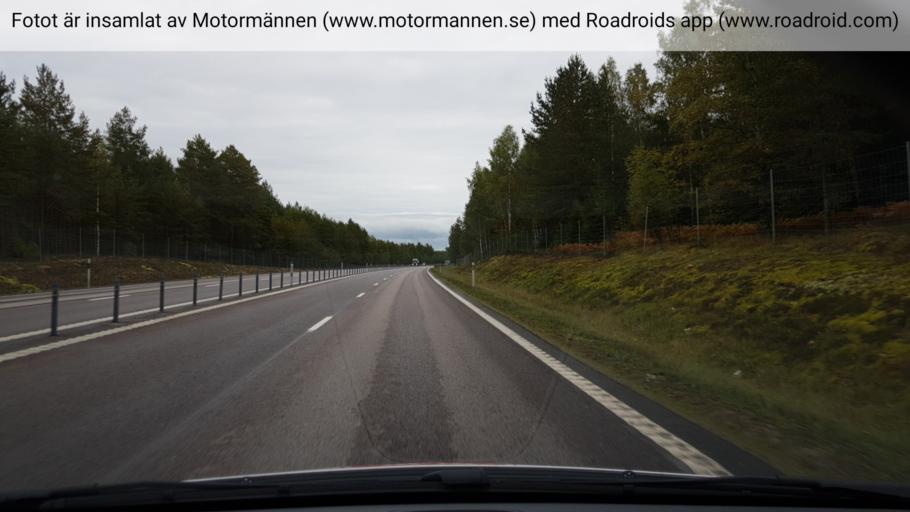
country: SE
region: Vaermland
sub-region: Karlstads Kommun
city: Valberg
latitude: 59.3826
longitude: 13.2110
